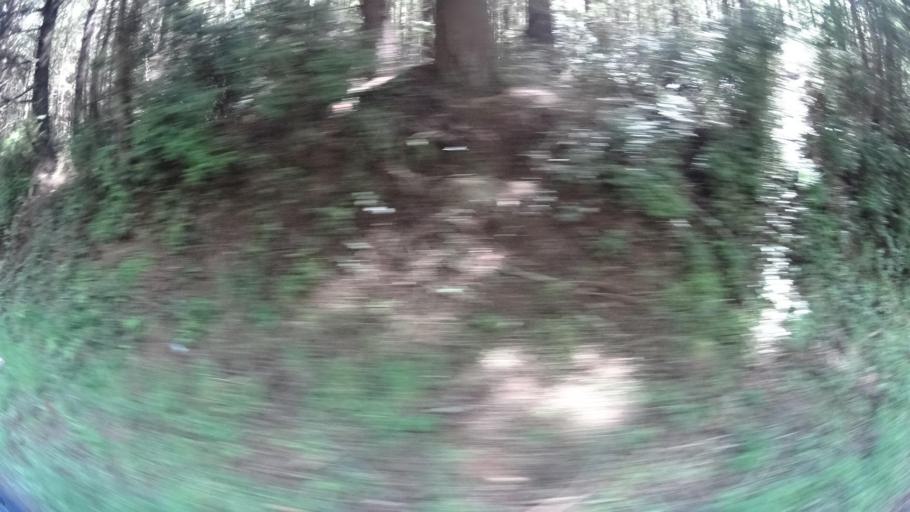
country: US
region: California
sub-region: Humboldt County
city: McKinleyville
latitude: 40.9584
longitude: -124.0711
